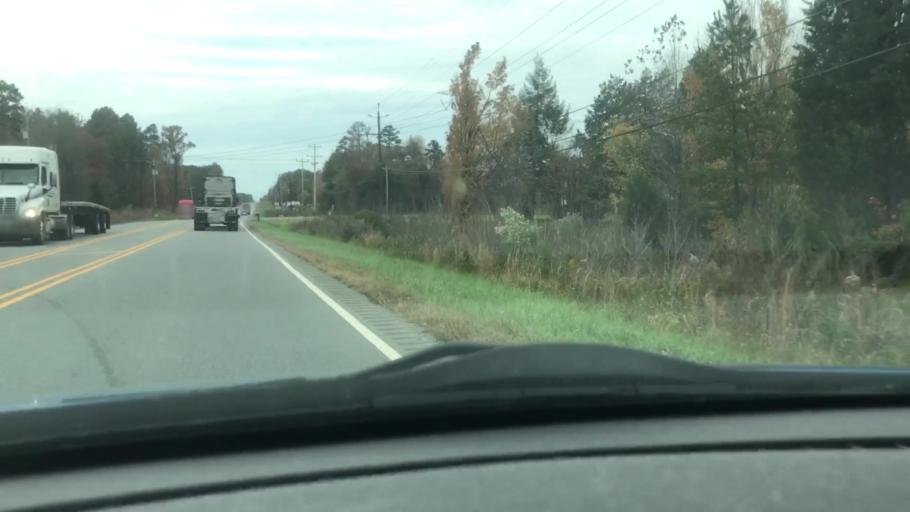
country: US
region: North Carolina
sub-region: Davidson County
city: Thomasville
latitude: 35.7792
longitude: -80.1204
